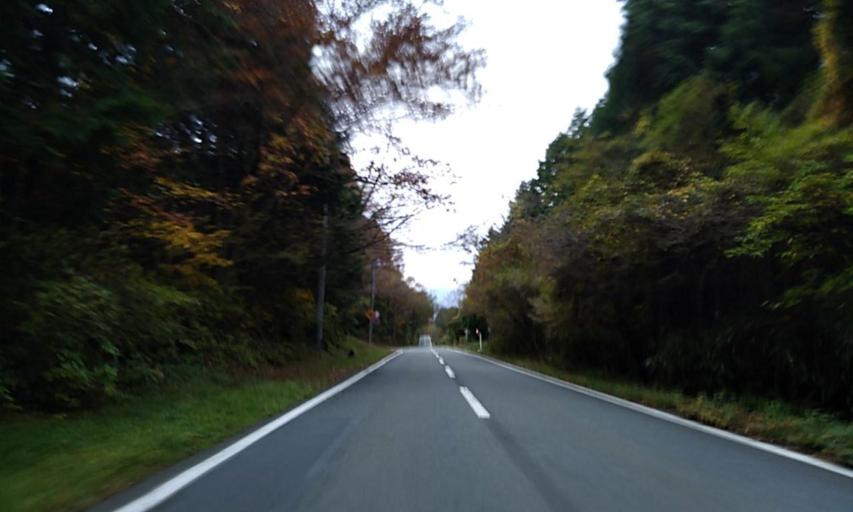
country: JP
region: Shizuoka
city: Gotemba
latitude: 35.2615
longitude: 138.8101
